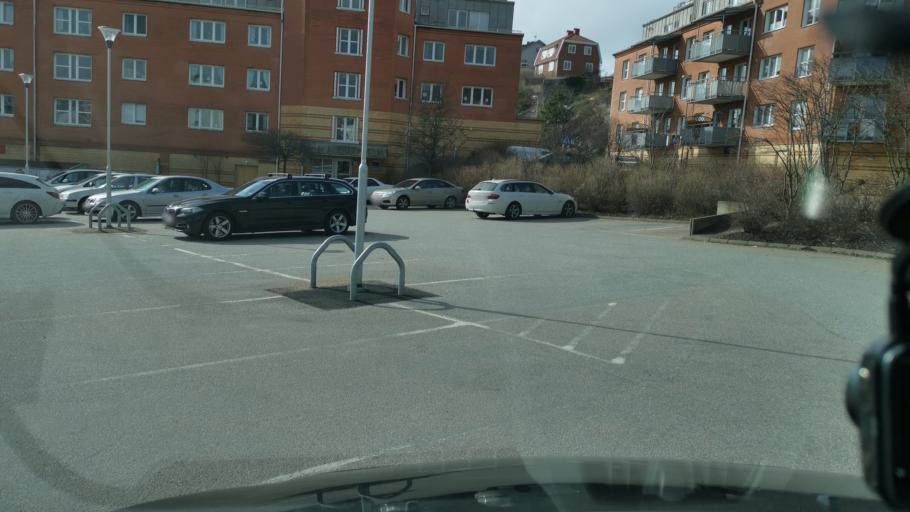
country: SE
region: Vaestra Goetaland
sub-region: Lysekils Kommun
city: Lysekil
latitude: 58.2768
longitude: 11.4408
